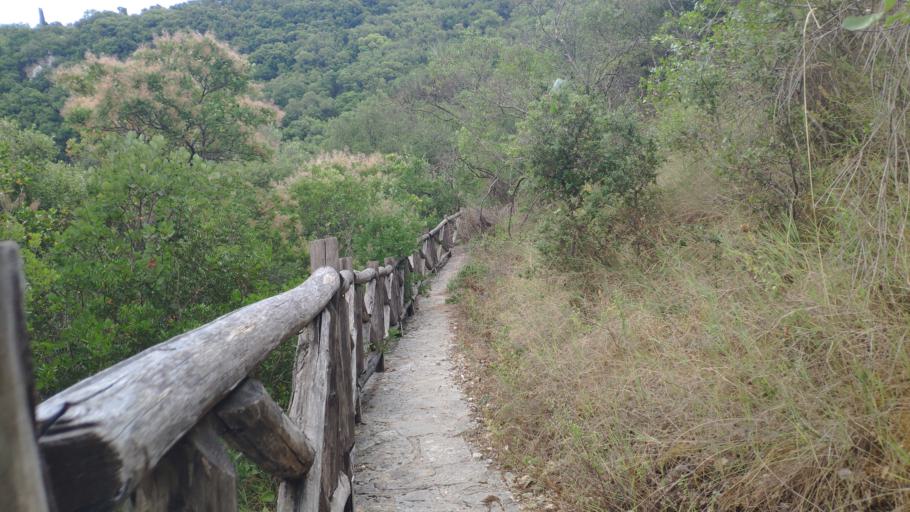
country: GR
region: Ionian Islands
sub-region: Lefkada
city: Lefkada
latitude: 38.8036
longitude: 20.6754
